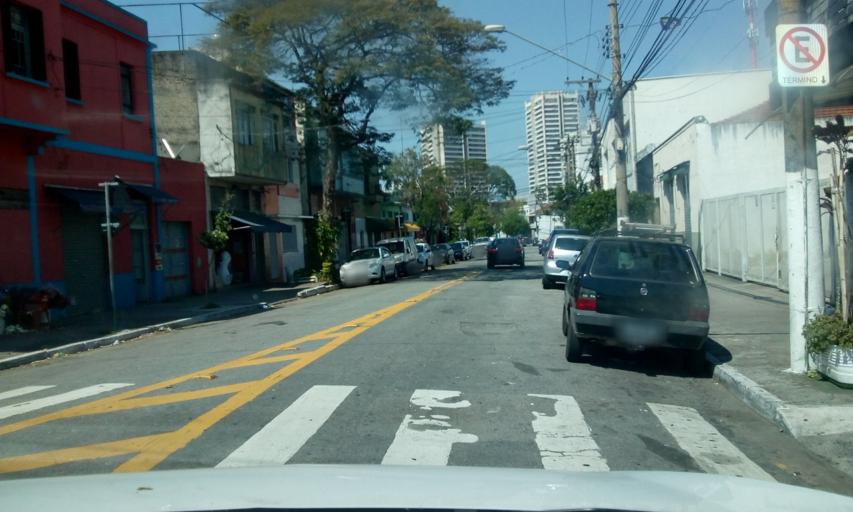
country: BR
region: Sao Paulo
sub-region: Osasco
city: Osasco
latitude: -23.5143
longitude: -46.7214
